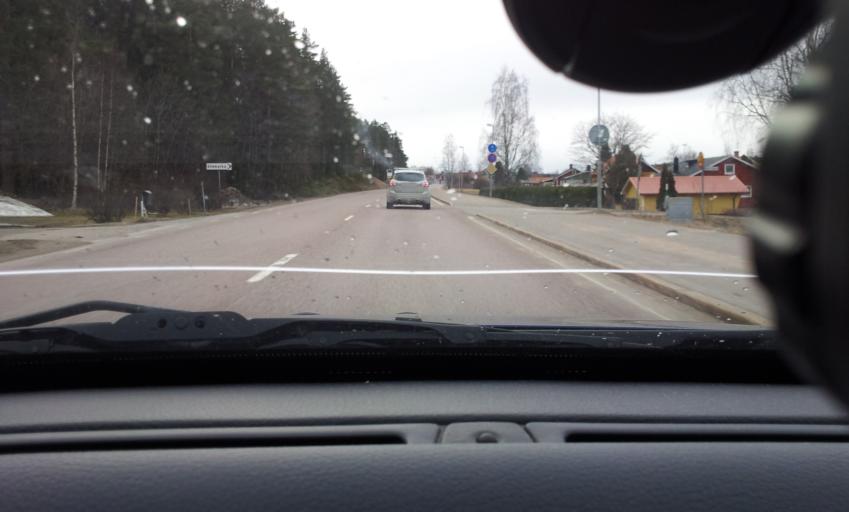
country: SE
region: Gaevleborg
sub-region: Ljusdals Kommun
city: Farila
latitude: 61.8008
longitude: 15.8589
